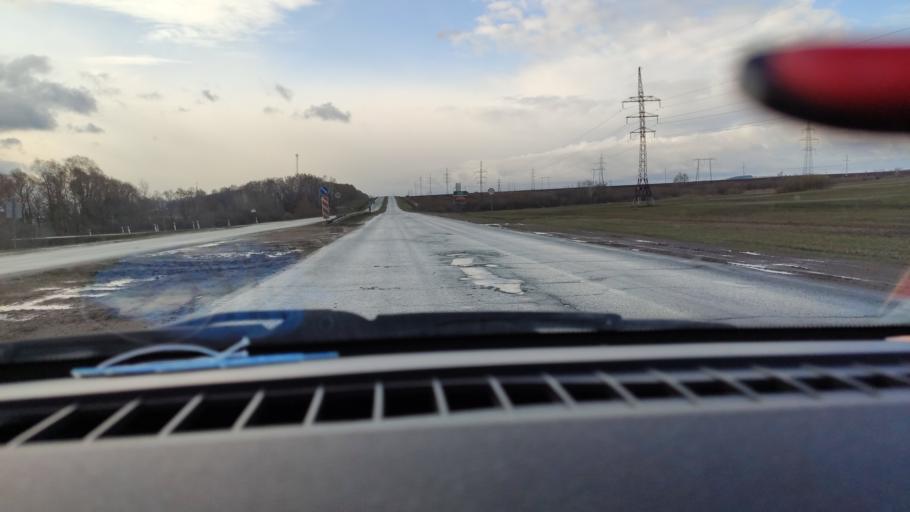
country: RU
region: Tatarstan
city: Zainsk
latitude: 55.1736
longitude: 52.0062
